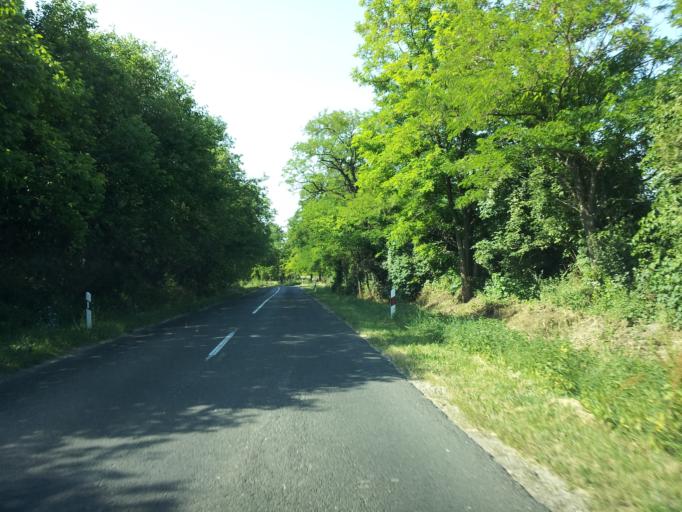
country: HU
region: Fejer
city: Lovasbereny
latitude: 47.3785
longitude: 18.5820
